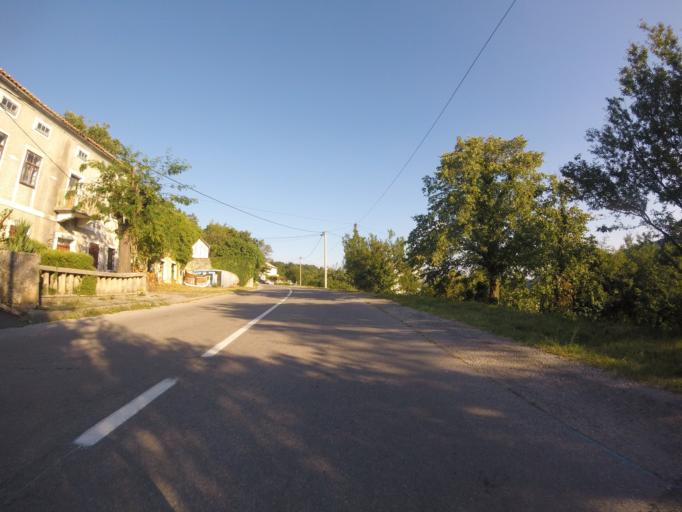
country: HR
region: Primorsko-Goranska
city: Selce
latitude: 45.1788
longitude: 14.7392
